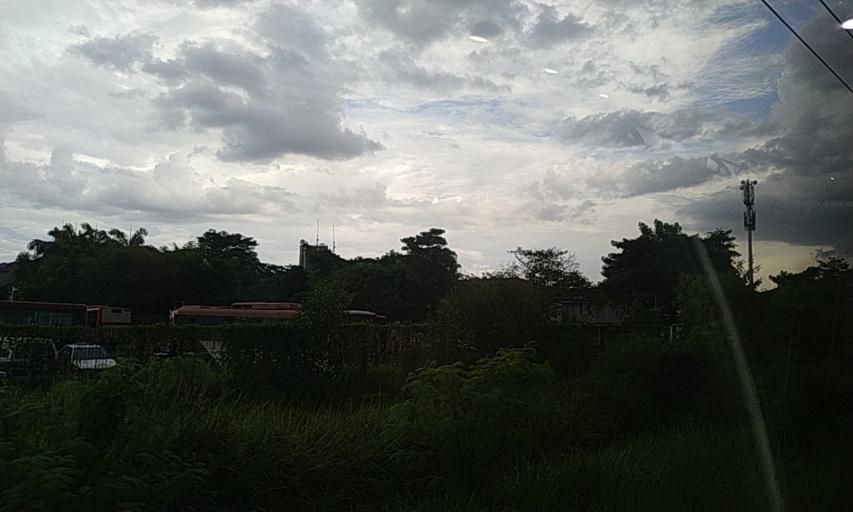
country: MY
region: Kuala Lumpur
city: Kuala Lumpur
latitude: 3.2173
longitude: 101.6724
